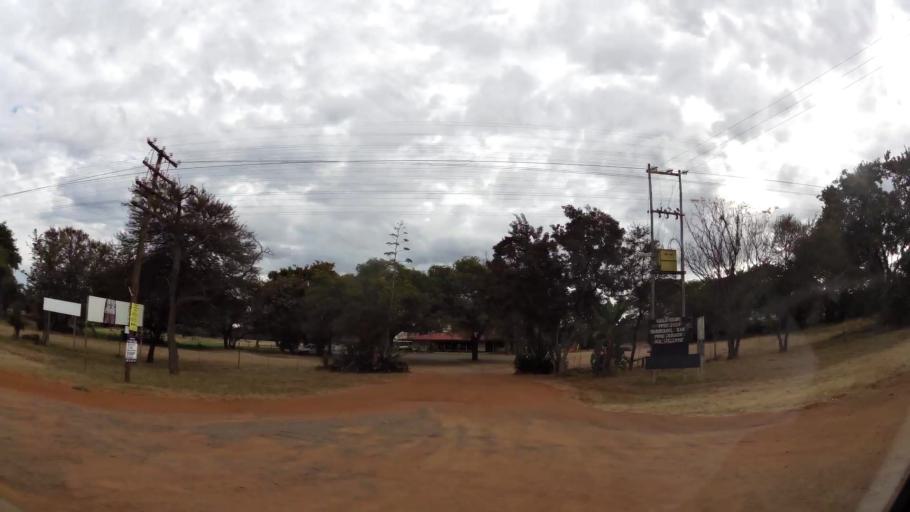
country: ZA
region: Limpopo
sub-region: Waterberg District Municipality
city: Modimolle
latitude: -24.5097
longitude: 28.7051
